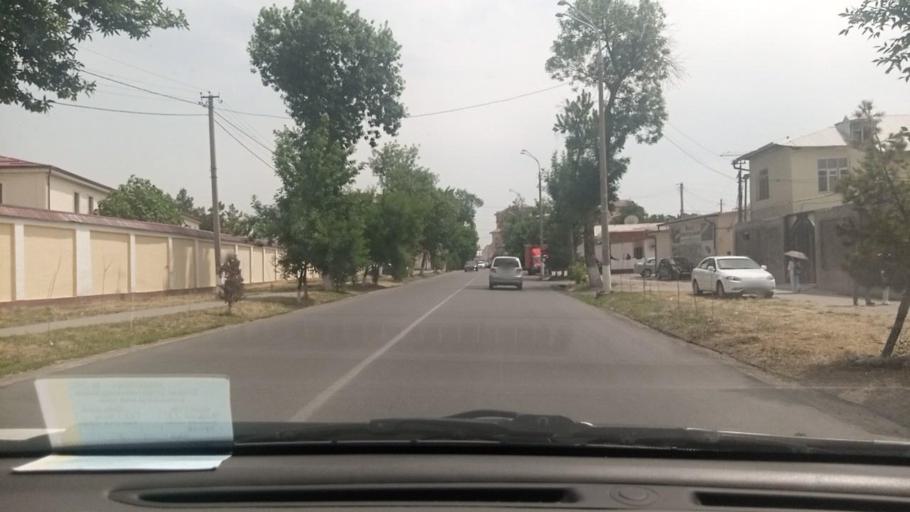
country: UZ
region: Toshkent Shahri
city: Tashkent
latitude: 41.2828
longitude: 69.2846
